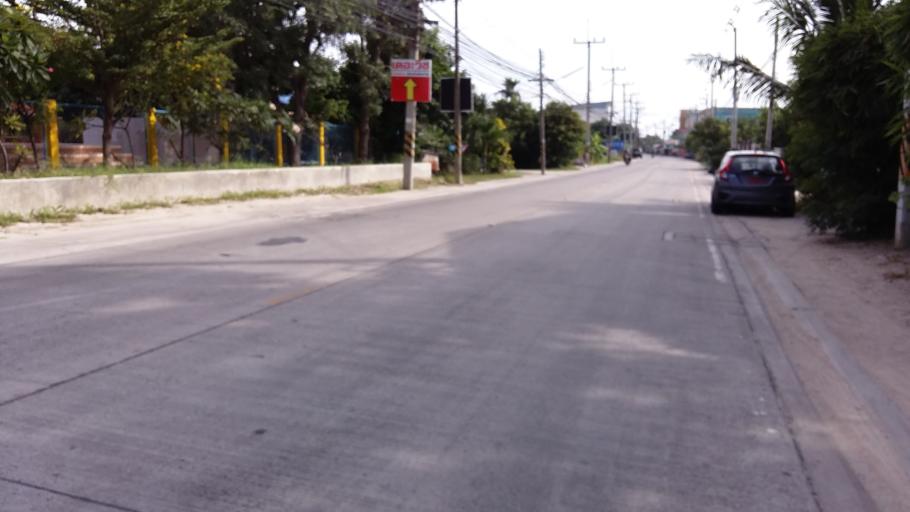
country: TH
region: Chon Buri
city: Chon Buri
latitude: 13.3128
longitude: 100.9312
